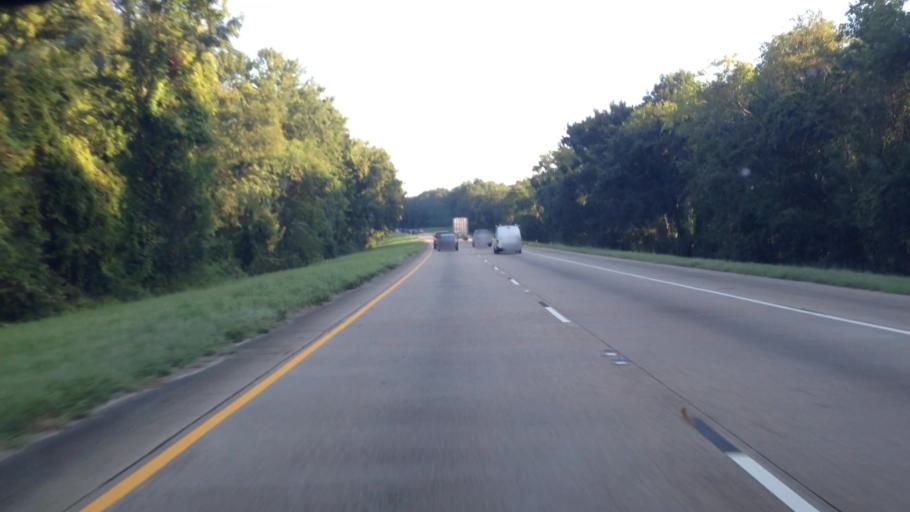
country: US
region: Louisiana
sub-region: Ascension Parish
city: Prairieville
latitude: 30.3037
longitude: -90.9929
